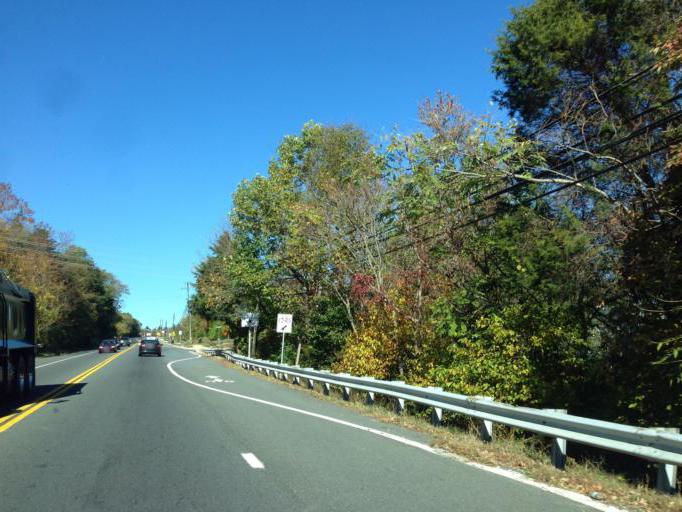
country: US
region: Maryland
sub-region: Montgomery County
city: Damascus
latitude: 39.2705
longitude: -77.2167
